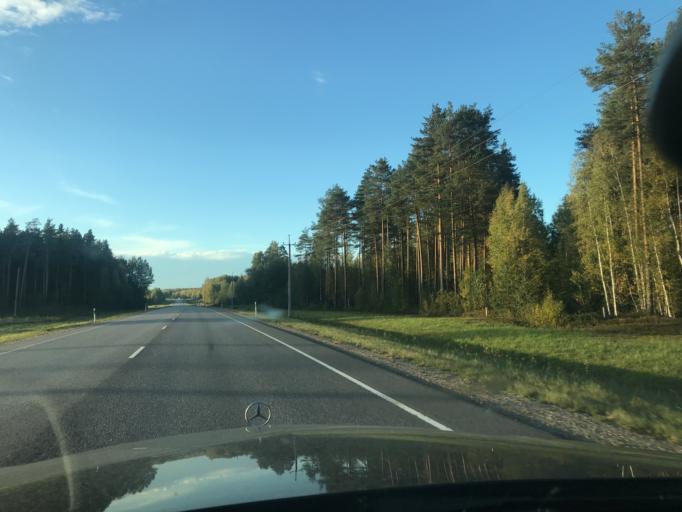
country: EE
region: Vorumaa
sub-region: Voru linn
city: Voru
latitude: 57.8402
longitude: 27.0540
